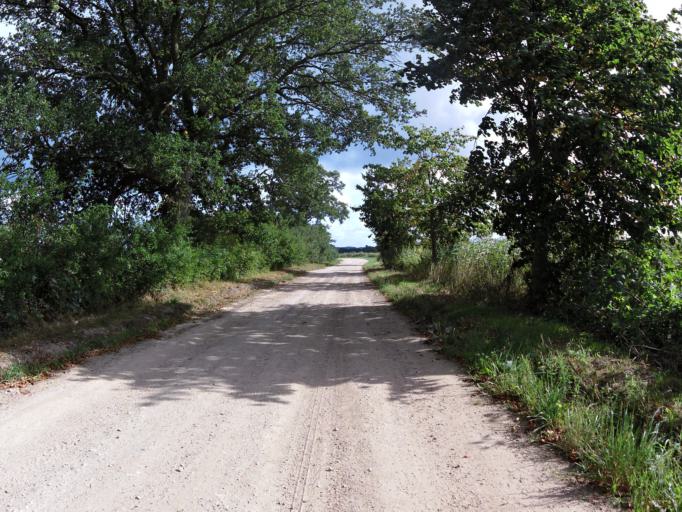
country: DE
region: Mecklenburg-Vorpommern
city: Loddin
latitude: 53.9871
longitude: 14.0587
